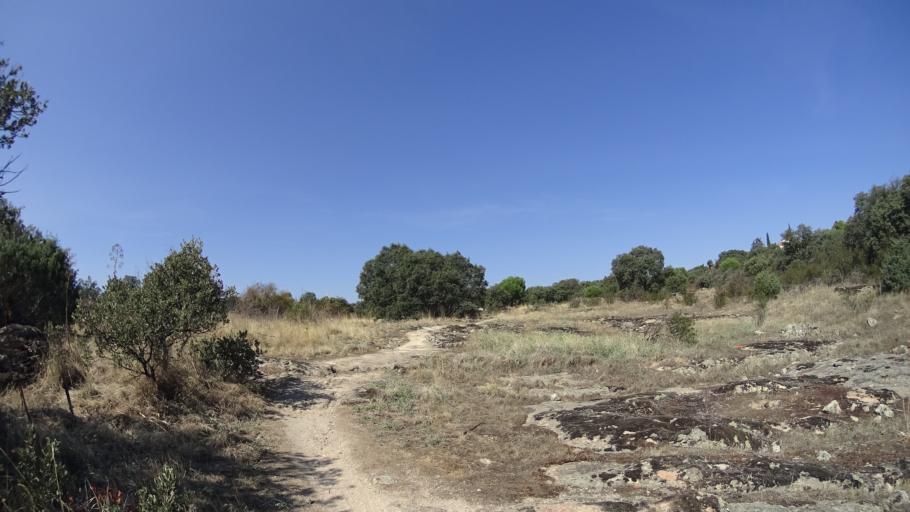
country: ES
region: Madrid
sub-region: Provincia de Madrid
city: Galapagar
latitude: 40.5846
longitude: -3.9772
